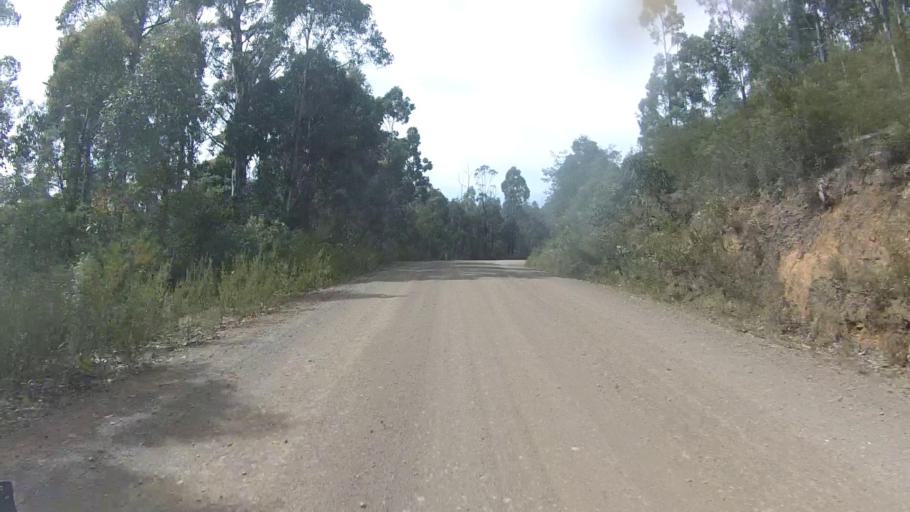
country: AU
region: Tasmania
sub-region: Sorell
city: Sorell
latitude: -42.7545
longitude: 147.8291
